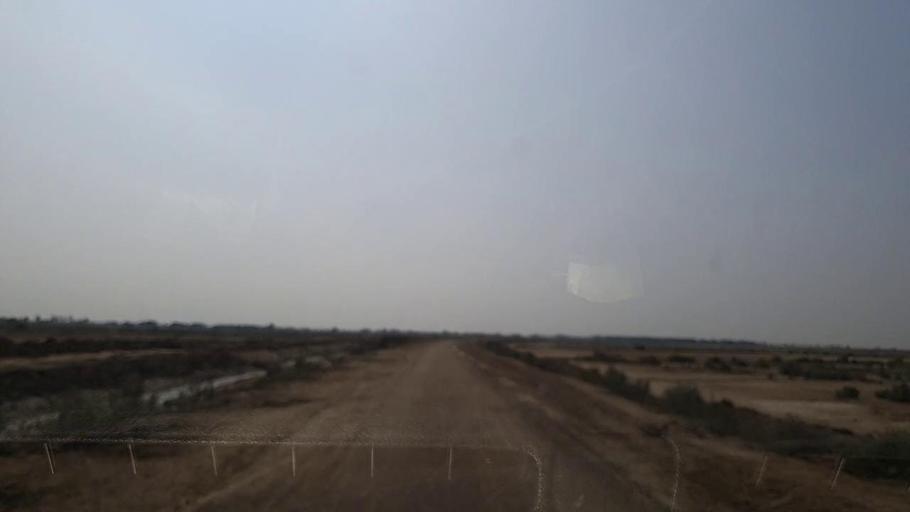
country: PK
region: Sindh
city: Mirpur Sakro
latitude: 24.5359
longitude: 67.7830
